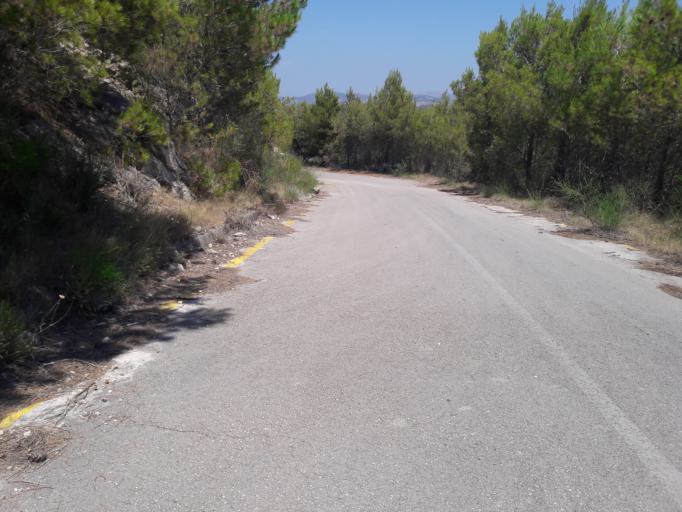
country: HR
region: Sibensko-Kniniska
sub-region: Grad Sibenik
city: Sibenik
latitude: 43.7022
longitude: 15.8463
